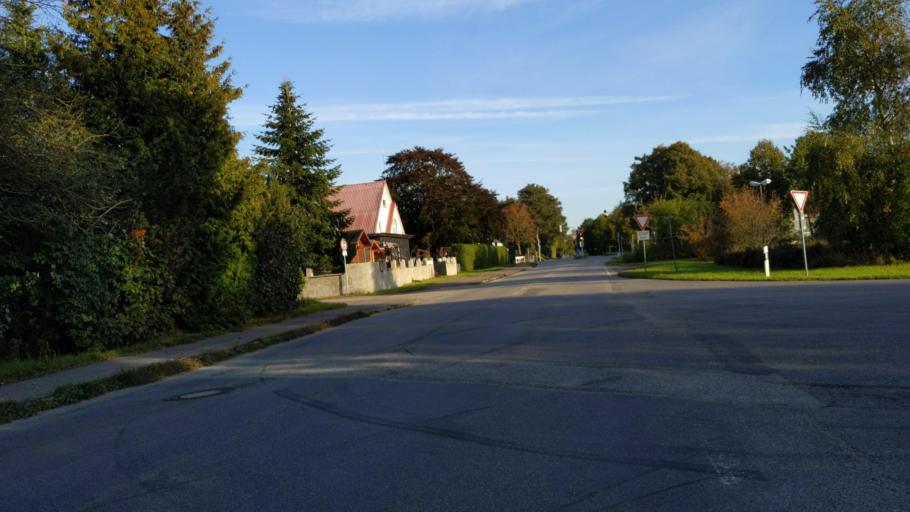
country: DE
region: Schleswig-Holstein
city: Susel
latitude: 54.0831
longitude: 10.6976
